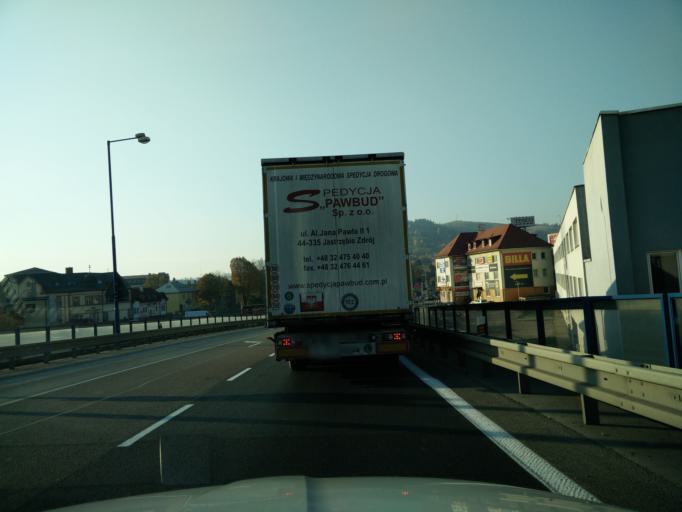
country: SK
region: Zilinsky
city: Cadca
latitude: 49.4401
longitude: 18.7916
